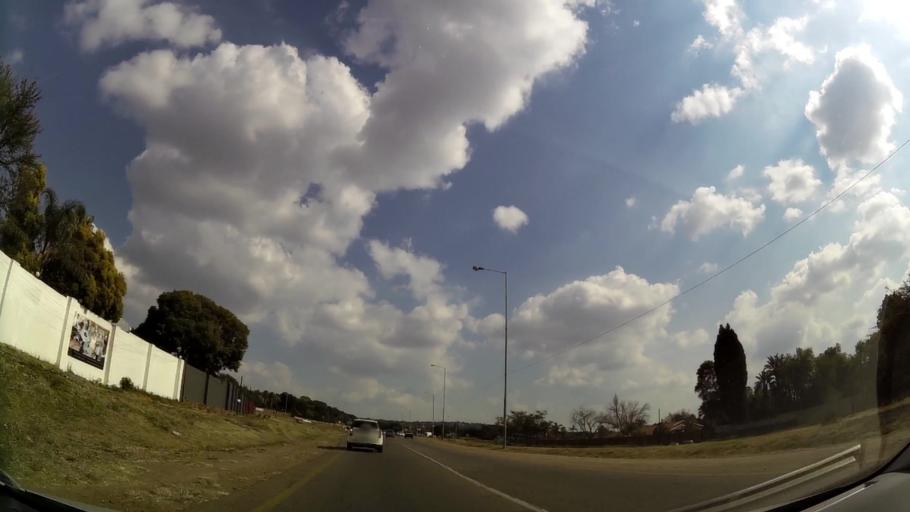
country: ZA
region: Gauteng
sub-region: City of Tshwane Metropolitan Municipality
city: Centurion
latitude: -25.8040
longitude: 28.2980
